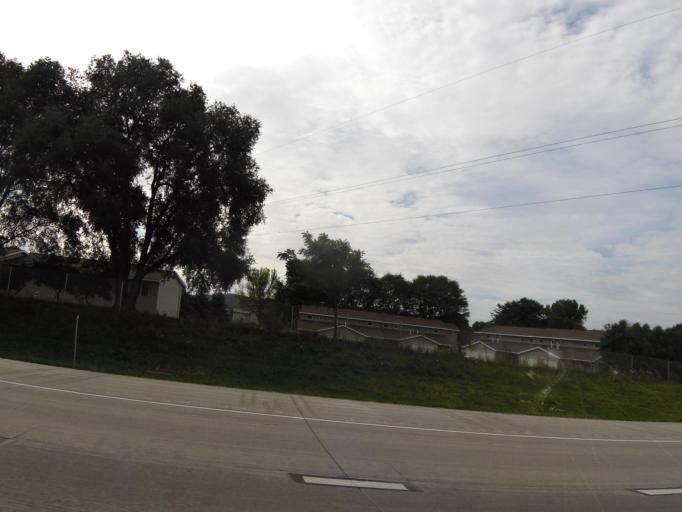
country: US
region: Wisconsin
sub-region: La Crosse County
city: Onalaska
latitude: 43.8770
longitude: -91.1992
